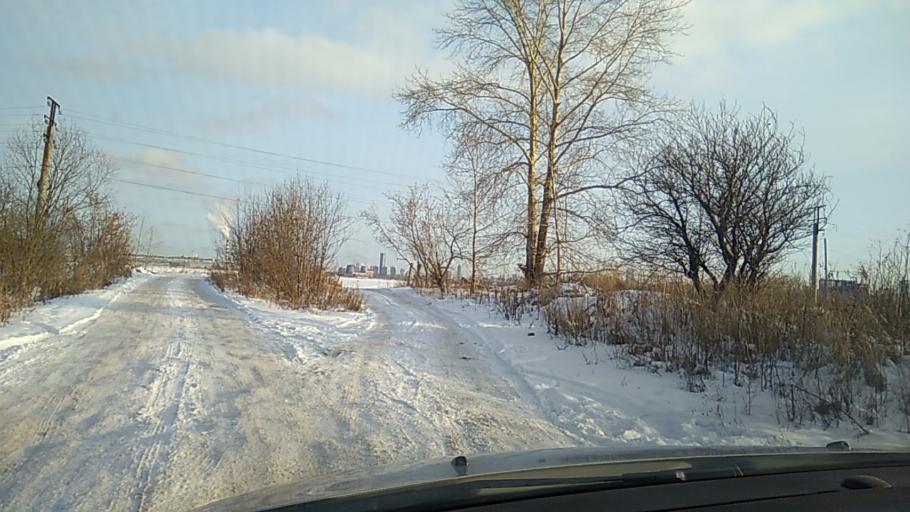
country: RU
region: Sverdlovsk
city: Shirokaya Rechka
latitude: 56.8452
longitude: 60.5015
